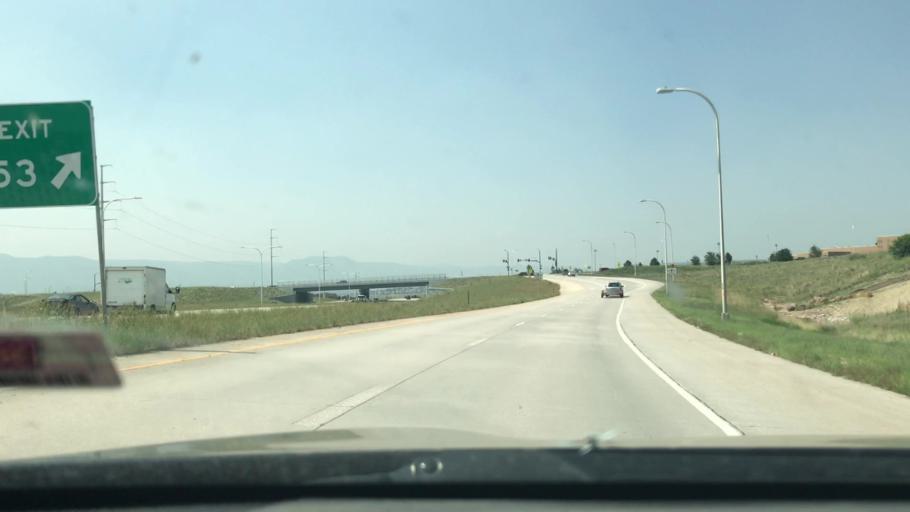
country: US
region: Colorado
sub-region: El Paso County
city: Black Forest
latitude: 38.9826
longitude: -104.7613
